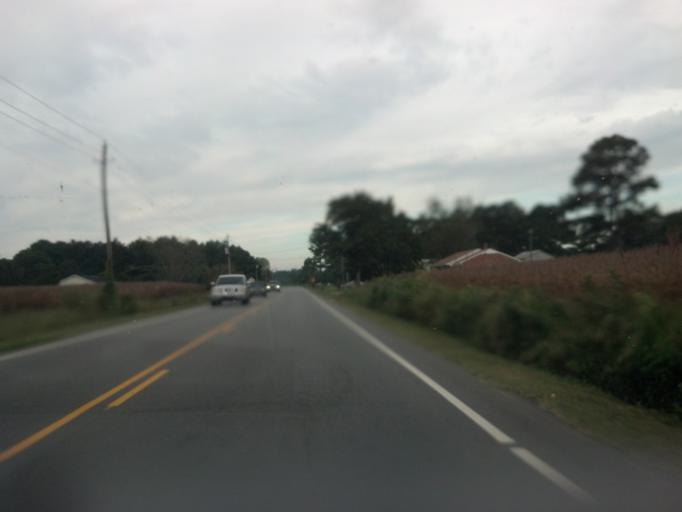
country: US
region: North Carolina
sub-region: Pitt County
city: Ayden
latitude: 35.4768
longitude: -77.4550
